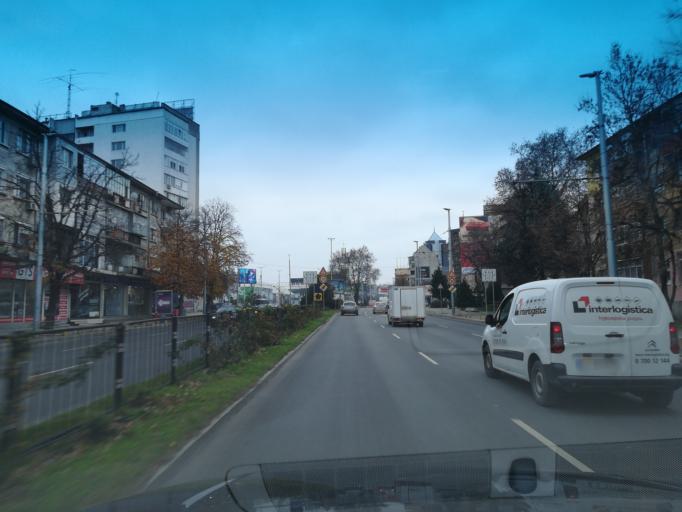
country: BG
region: Plovdiv
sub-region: Obshtina Plovdiv
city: Plovdiv
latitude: 42.1606
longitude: 24.7483
